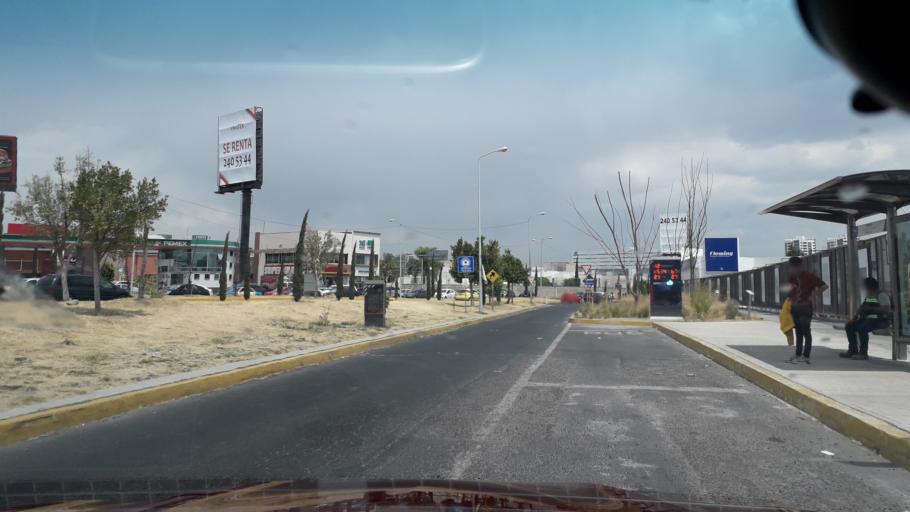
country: MX
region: Puebla
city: Tlazcalancingo
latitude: 19.0222
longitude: -98.2424
